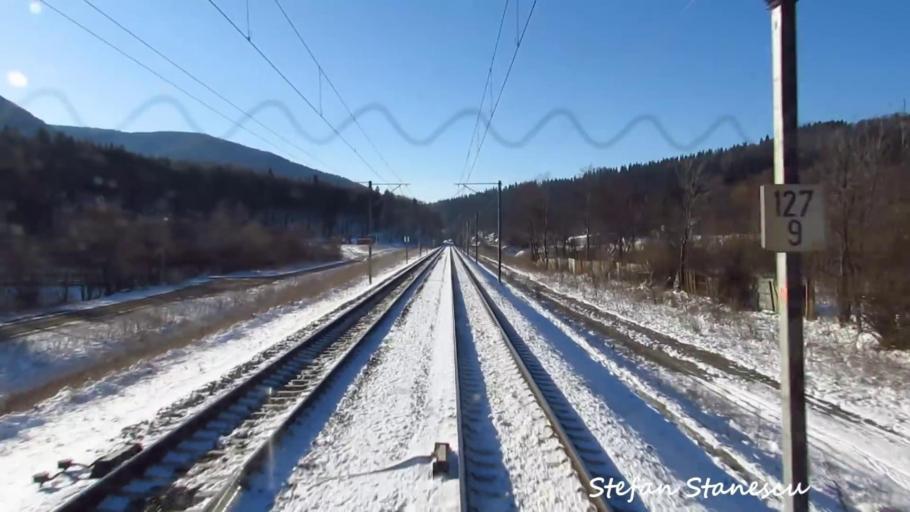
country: RO
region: Prahova
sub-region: Oras Busteni
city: Poiana Tapului
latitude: 45.3761
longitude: 25.5424
